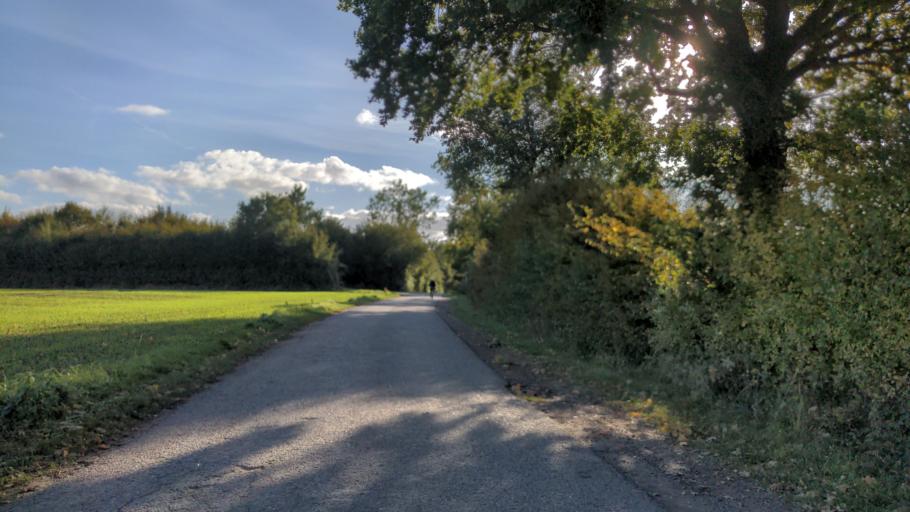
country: DE
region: Schleswig-Holstein
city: Manhagen
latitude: 54.1752
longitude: 10.9121
